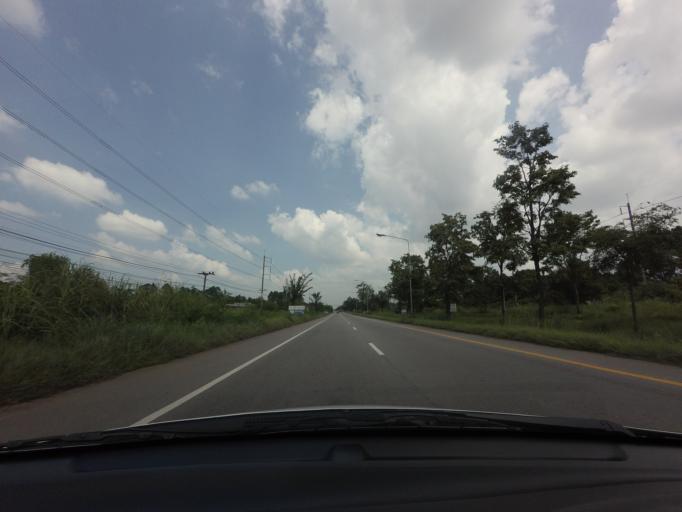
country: TH
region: Prachin Buri
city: Kabin Buri
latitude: 13.9417
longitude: 101.7049
